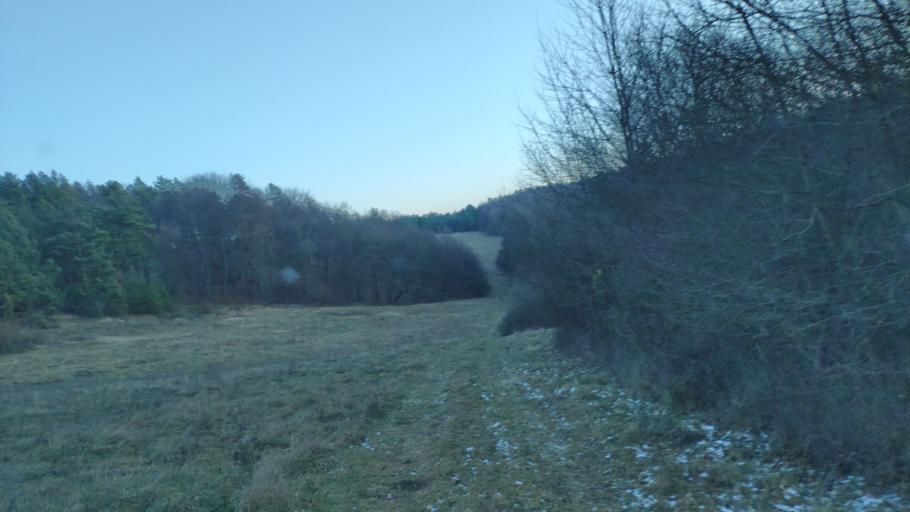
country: SK
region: Kosicky
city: Kosice
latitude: 48.8494
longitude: 21.2406
